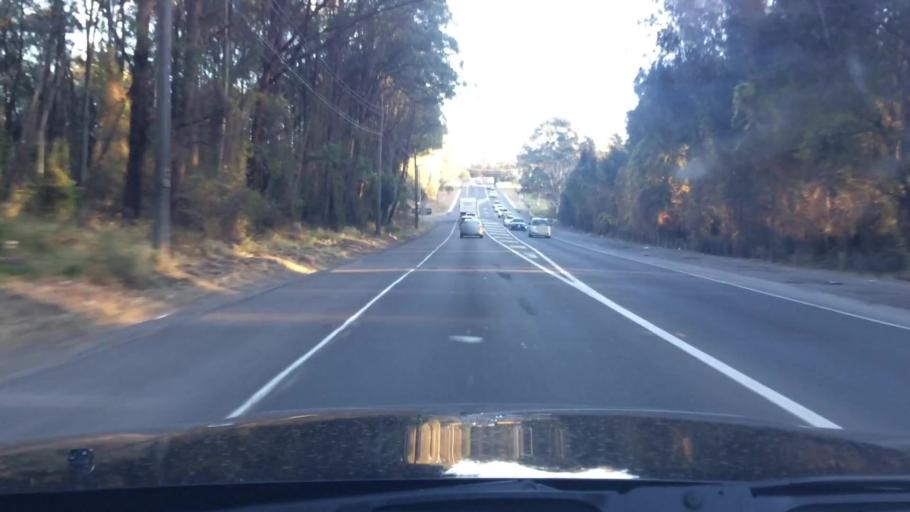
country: AU
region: New South Wales
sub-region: Fairfield
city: Carramar
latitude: -33.8970
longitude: 150.9729
